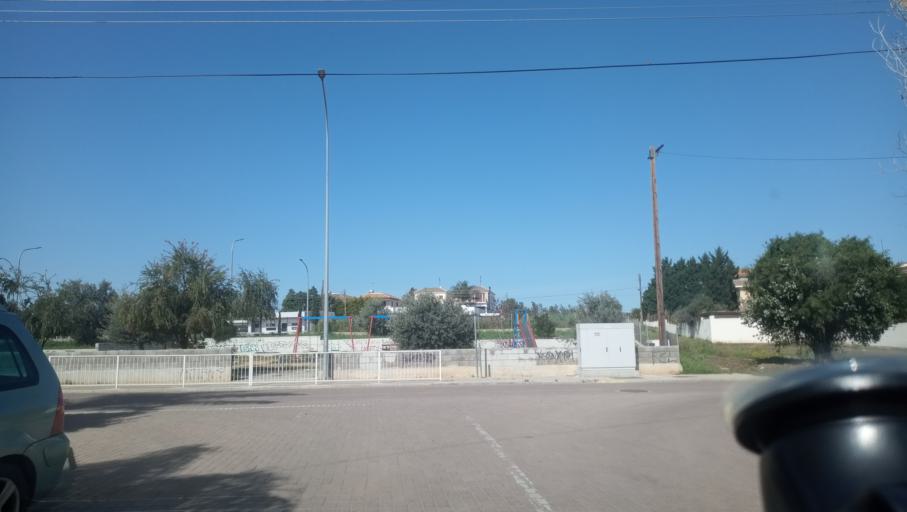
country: CY
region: Lefkosia
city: Tseri
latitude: 35.0917
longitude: 33.3067
